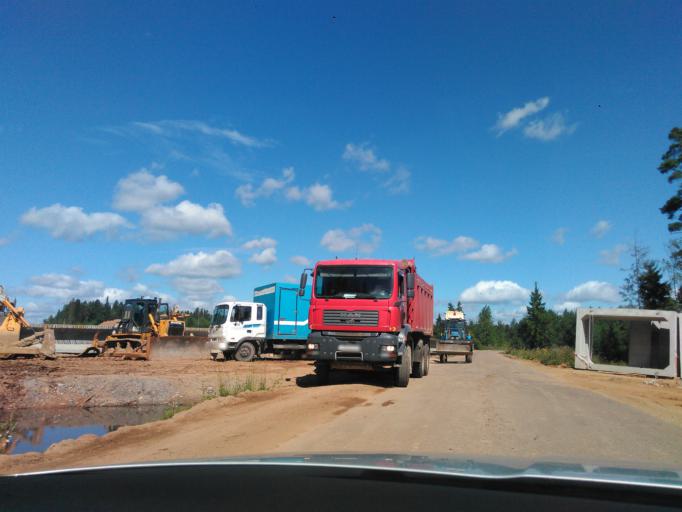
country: RU
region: Moskovskaya
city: Klin
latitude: 56.2081
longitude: 36.8108
